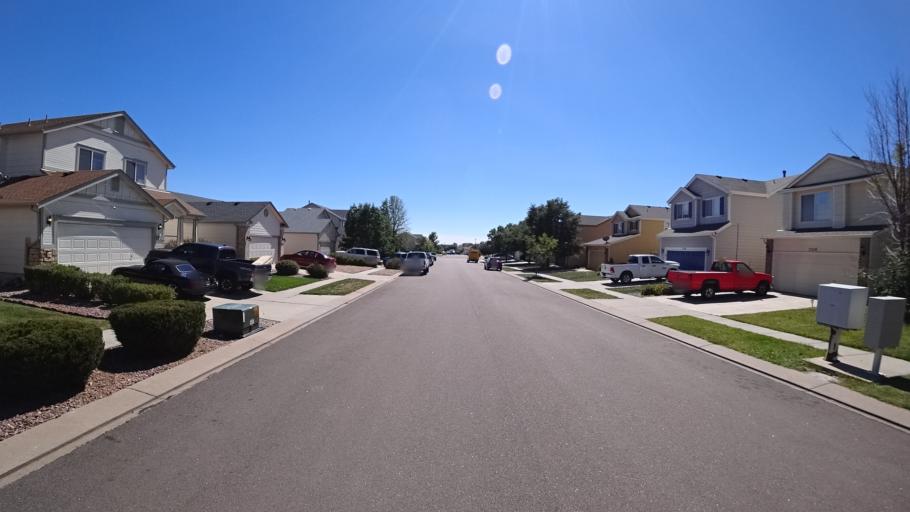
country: US
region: Colorado
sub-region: El Paso County
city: Security-Widefield
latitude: 38.7841
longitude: -104.7327
